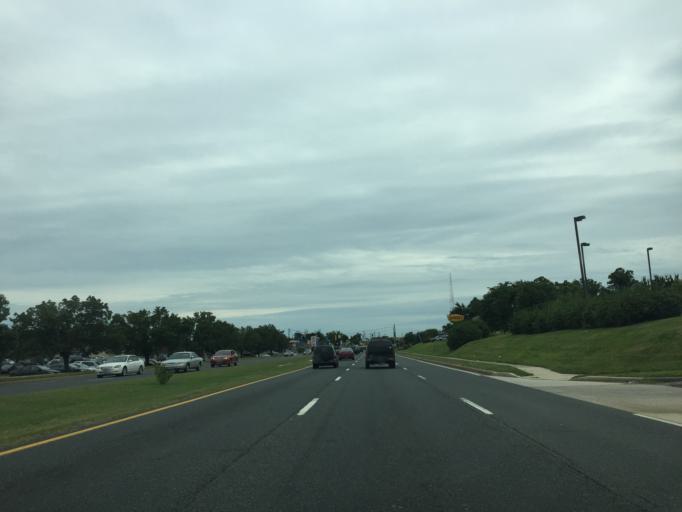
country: US
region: Maryland
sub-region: Baltimore County
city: Dundalk
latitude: 39.2771
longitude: -76.5043
